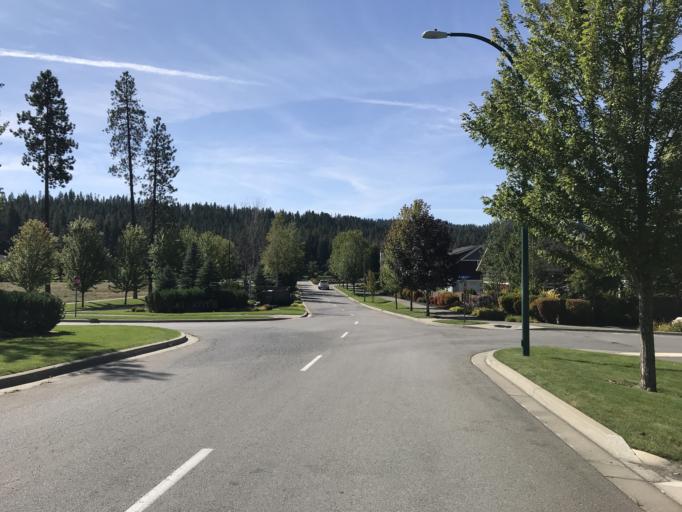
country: US
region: Idaho
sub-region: Kootenai County
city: Coeur d'Alene
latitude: 47.7020
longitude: -116.8397
